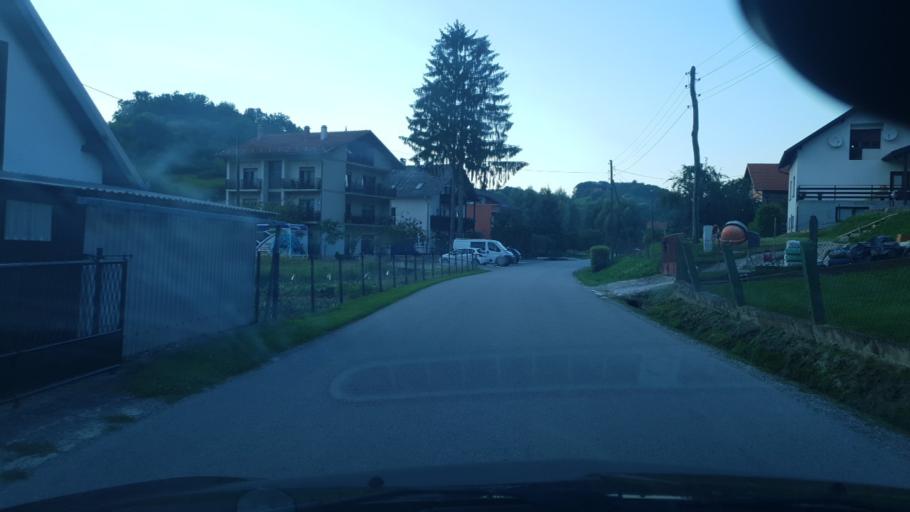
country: HR
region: Krapinsko-Zagorska
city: Zabok
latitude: 46.0302
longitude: 15.8981
